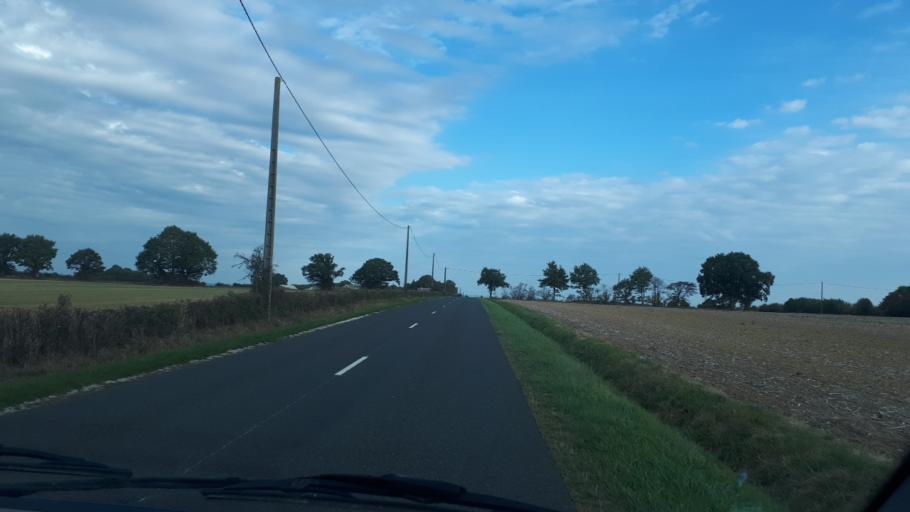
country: FR
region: Centre
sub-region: Departement du Loir-et-Cher
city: Mondoubleau
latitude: 47.9477
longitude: 0.9323
